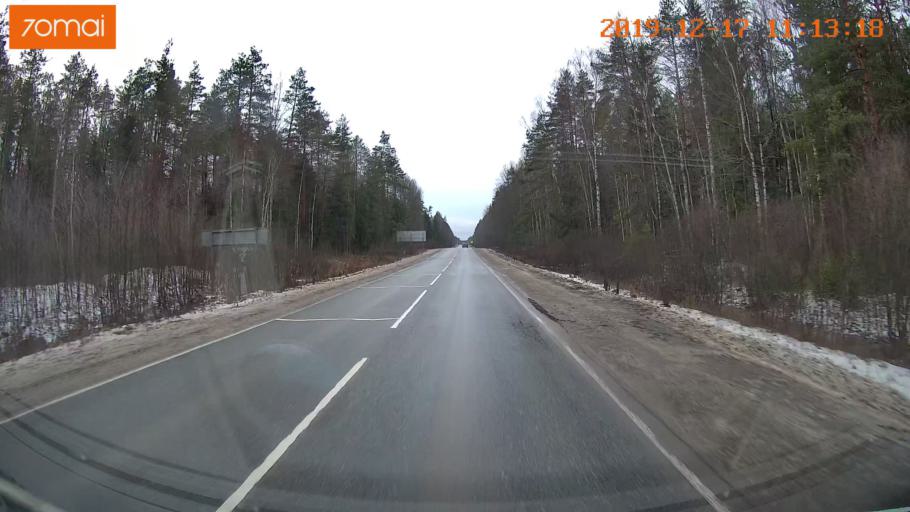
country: RU
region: Vladimir
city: Gus'-Khrustal'nyy
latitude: 55.5650
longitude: 40.6201
